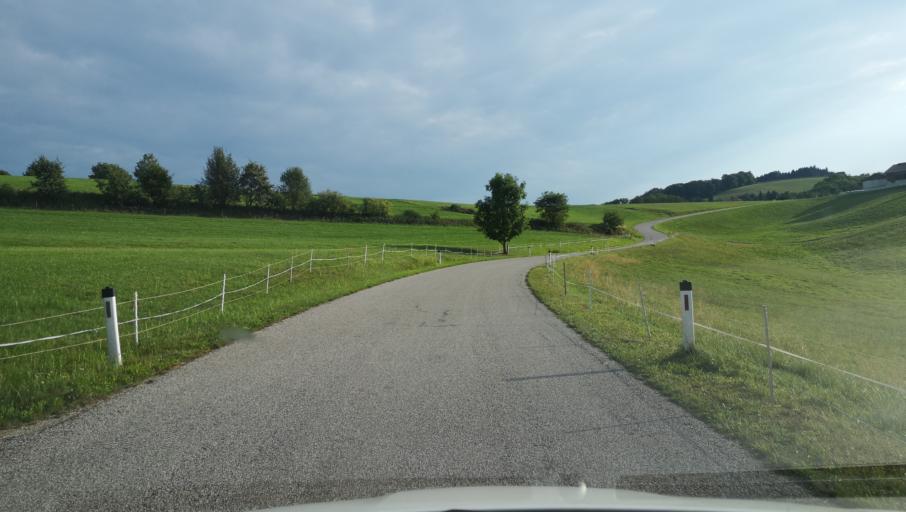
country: AT
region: Lower Austria
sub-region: Politischer Bezirk Amstetten
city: Sankt Georgen am Ybbsfelde
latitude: 48.1598
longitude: 14.9563
